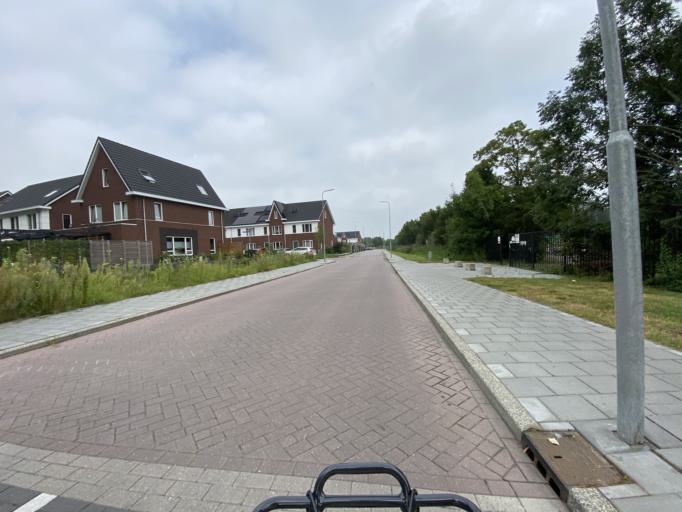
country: NL
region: North Holland
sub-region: Gemeente Weesp
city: Weesp
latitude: 52.3144
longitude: 5.0334
